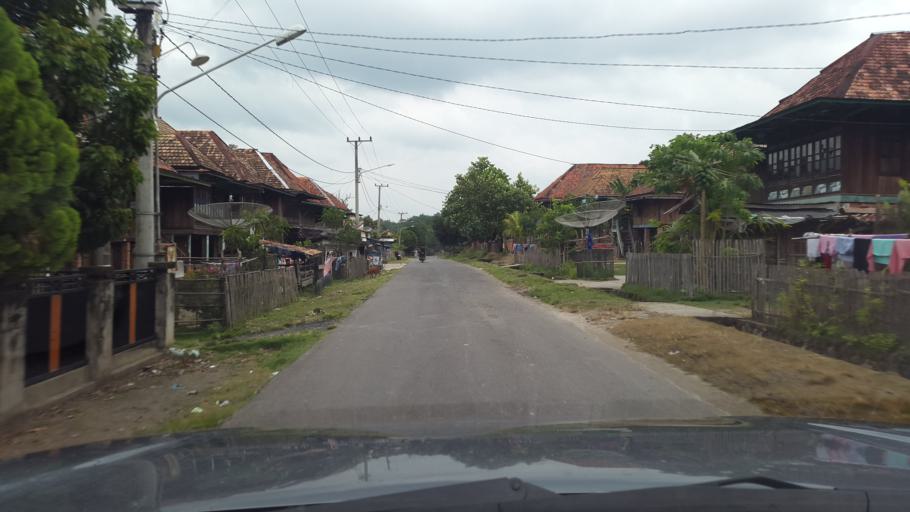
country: ID
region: South Sumatra
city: Gunungmenang
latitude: -3.1043
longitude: 103.9204
